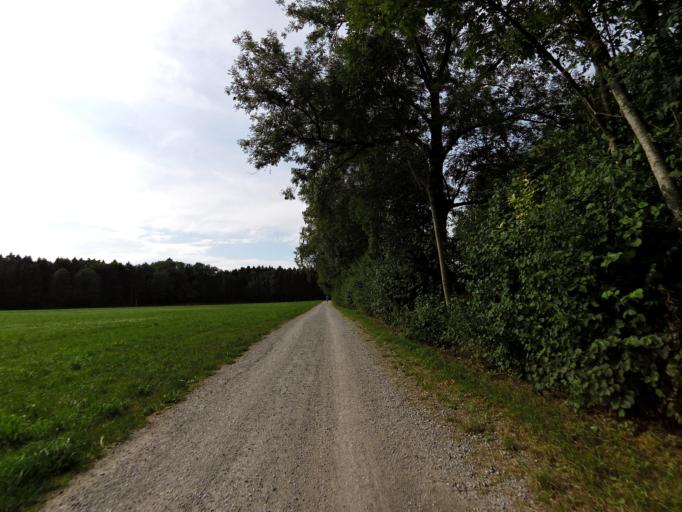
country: CH
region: Zurich
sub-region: Bezirk Buelach
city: Glattbrugg
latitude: 47.4394
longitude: 8.5554
